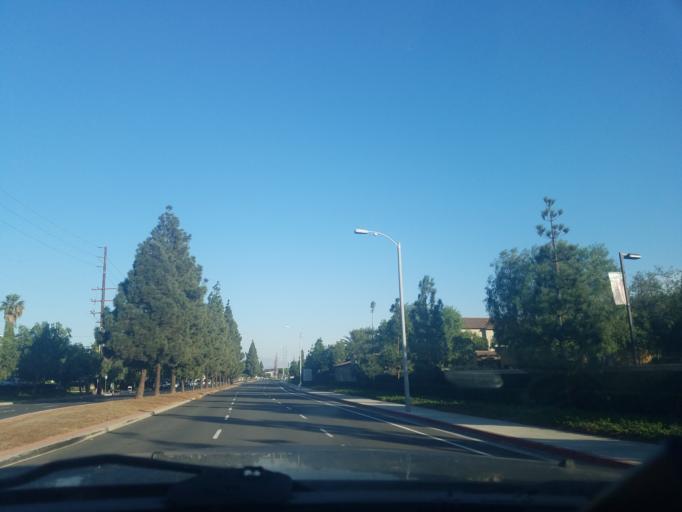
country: US
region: California
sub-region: Orange County
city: Santa Ana
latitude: 33.6940
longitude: -117.8760
